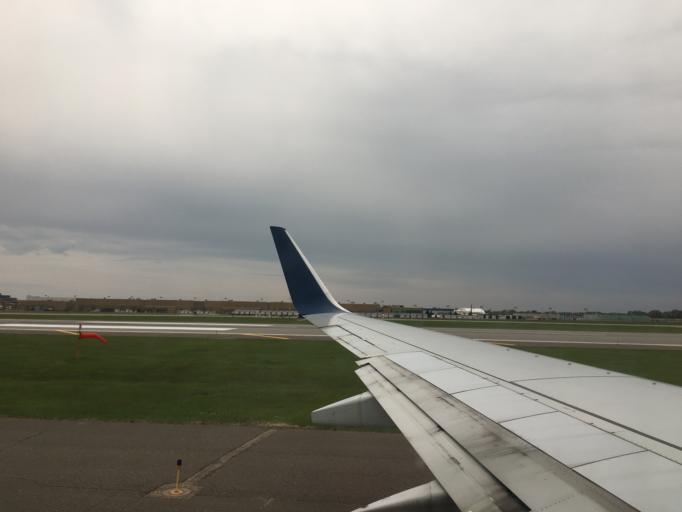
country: US
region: Minnesota
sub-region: Hennepin County
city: Richfield
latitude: 44.8875
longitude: -93.2302
